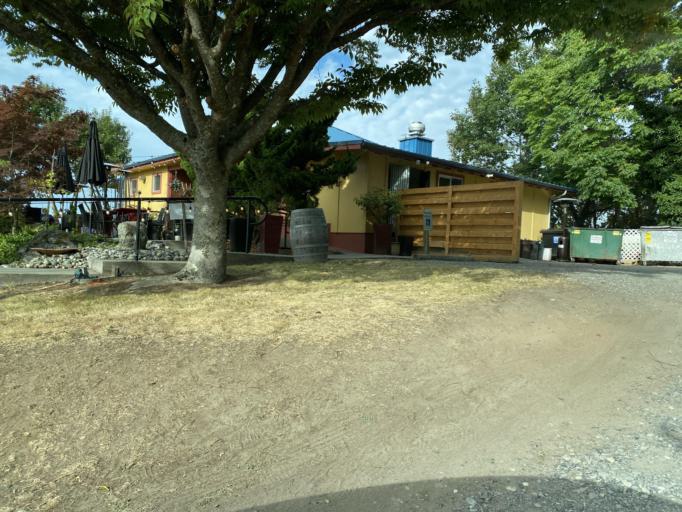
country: US
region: Washington
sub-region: Island County
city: Freeland
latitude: 48.0128
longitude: -122.5383
